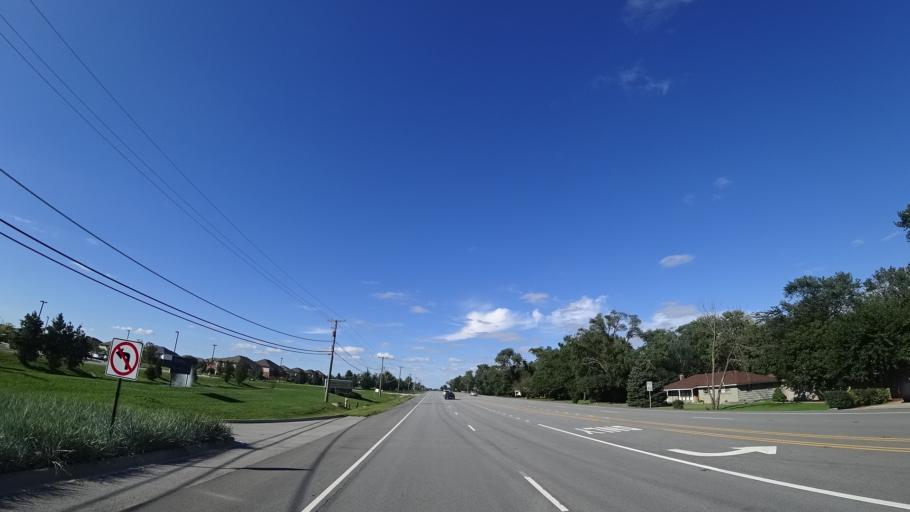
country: US
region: Illinois
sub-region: Cook County
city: Country Club Hills
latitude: 41.5586
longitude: -87.7333
